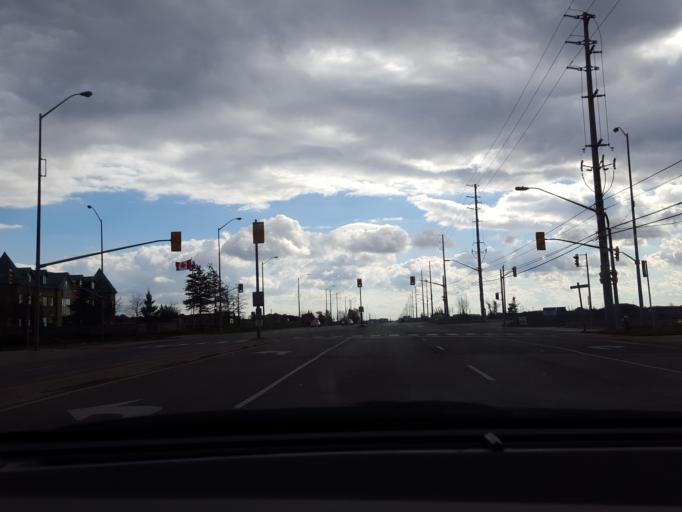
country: CA
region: Ontario
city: Brampton
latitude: 43.6381
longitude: -79.7906
